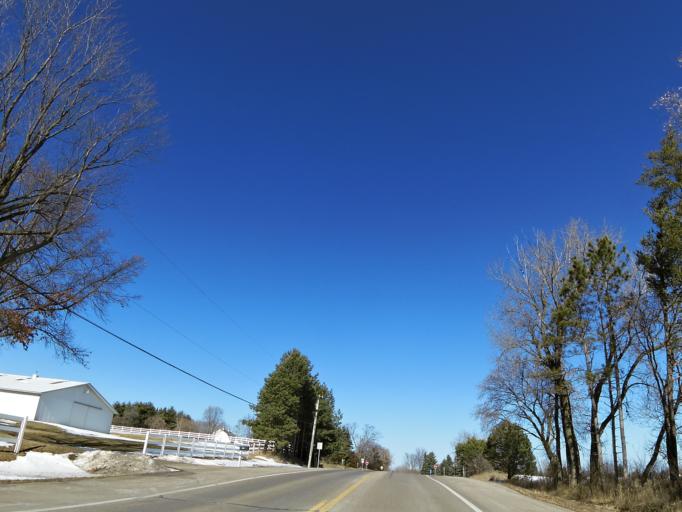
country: US
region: Minnesota
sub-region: Washington County
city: Grant
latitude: 45.0562
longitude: -92.8834
